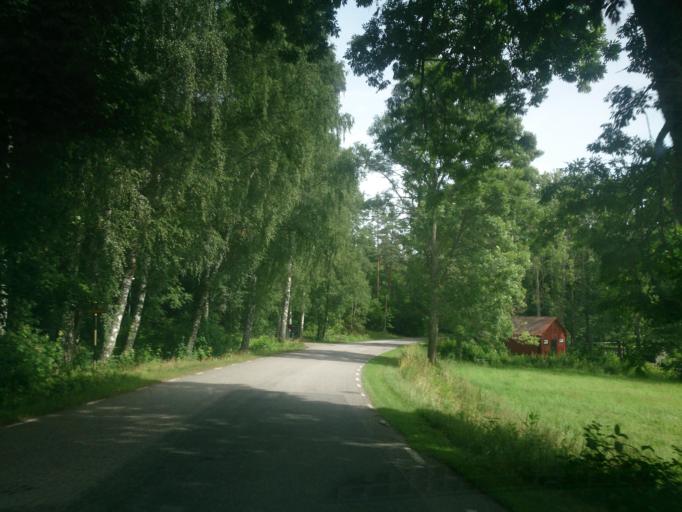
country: SE
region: OEstergoetland
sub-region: Soderkopings Kommun
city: Soederkoeping
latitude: 58.3025
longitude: 16.2597
